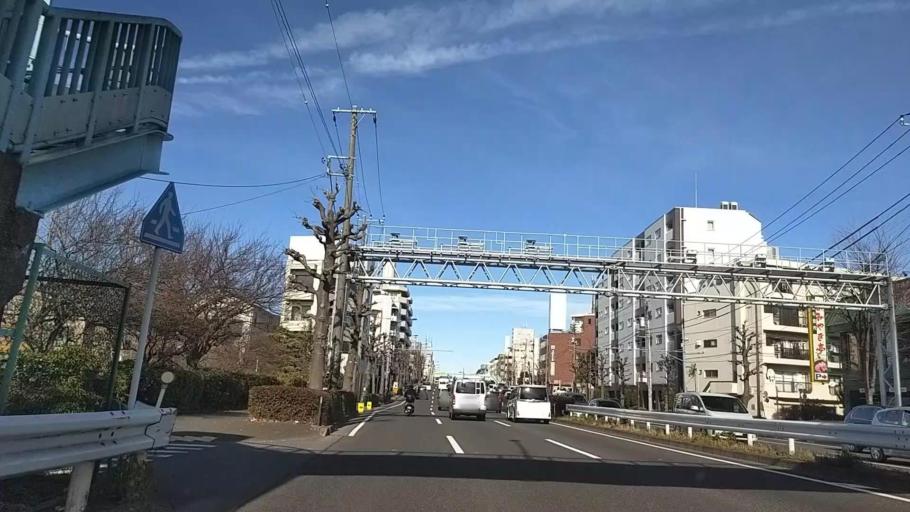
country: JP
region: Tokyo
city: Mitaka-shi
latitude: 35.6463
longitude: 139.6177
